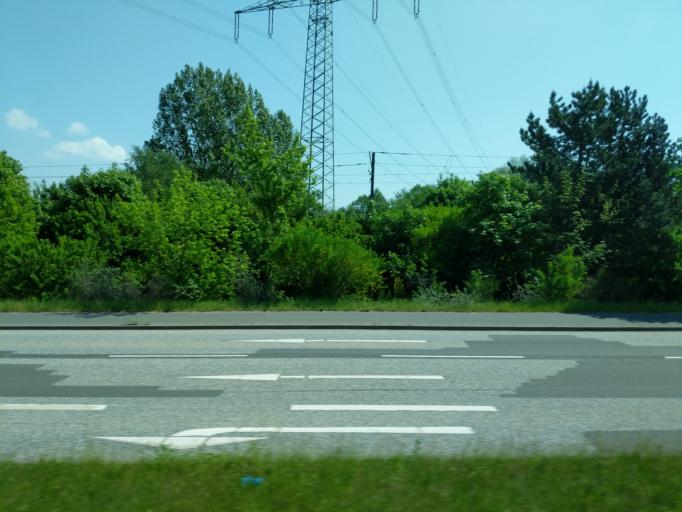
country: DE
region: Mecklenburg-Vorpommern
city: Feldstadt
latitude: 53.5852
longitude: 11.4002
